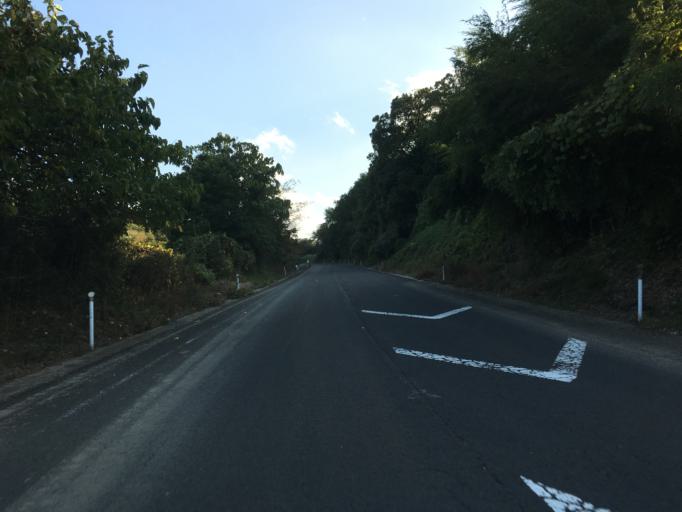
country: JP
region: Fukushima
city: Fukushima-shi
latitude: 37.6547
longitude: 140.5449
